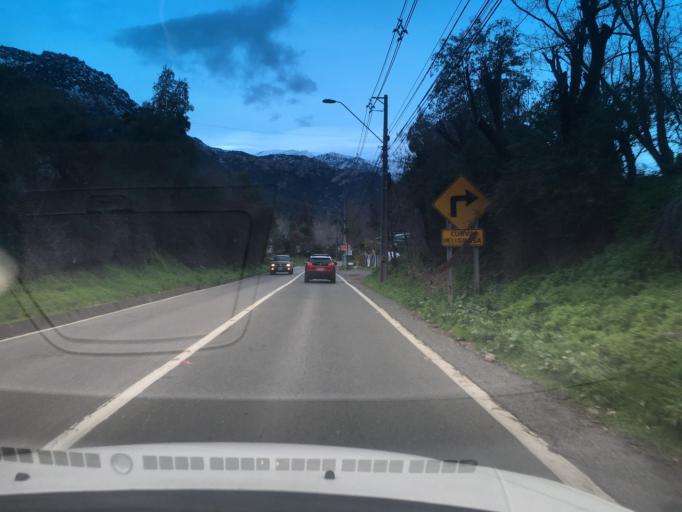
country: CL
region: Santiago Metropolitan
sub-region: Provincia de Cordillera
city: Puente Alto
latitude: -33.5796
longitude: -70.4110
